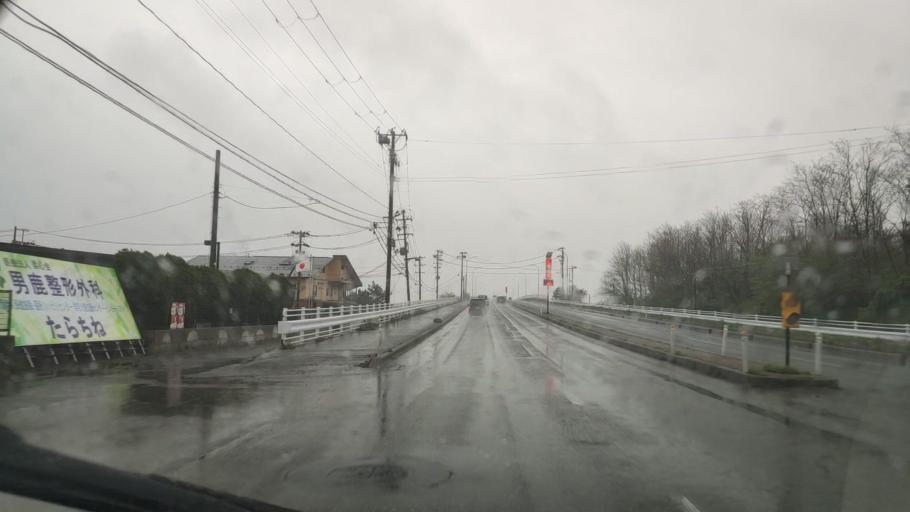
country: JP
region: Akita
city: Tenno
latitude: 39.8979
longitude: 139.9476
